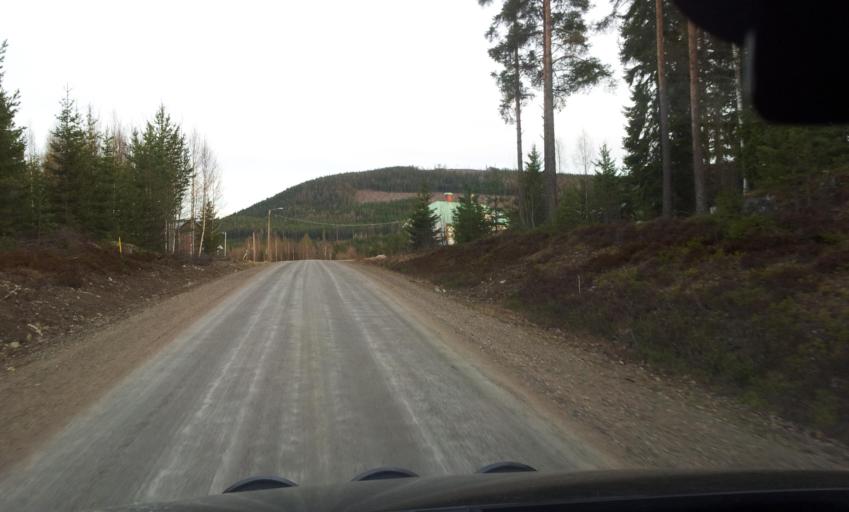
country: SE
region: Gaevleborg
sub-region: Ljusdals Kommun
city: Farila
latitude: 62.0713
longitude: 15.7791
